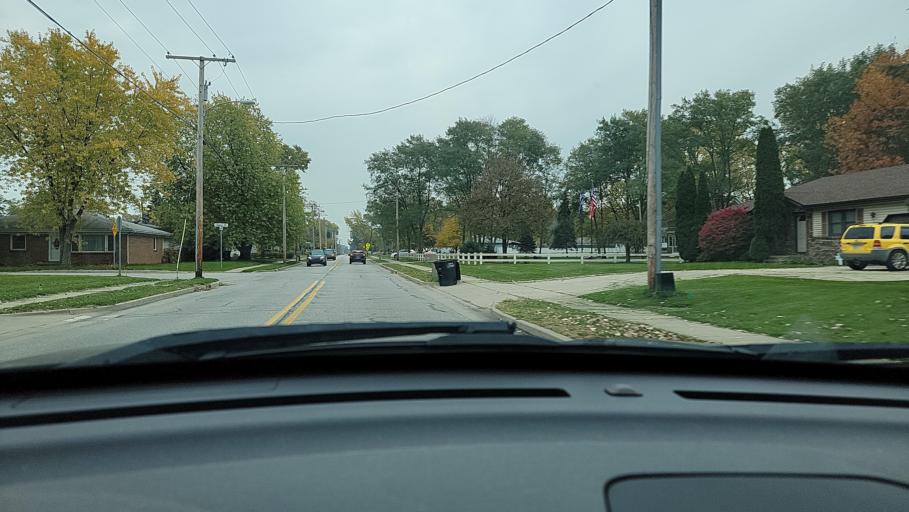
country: US
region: Indiana
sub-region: Lake County
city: Lake Station
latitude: 41.5651
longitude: -87.2167
